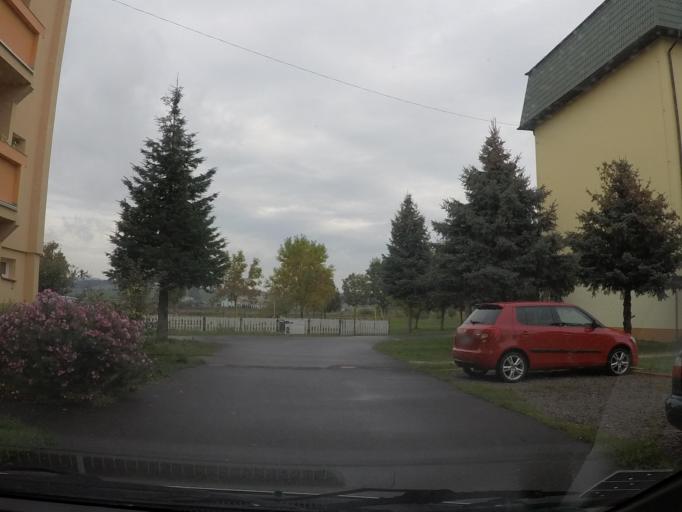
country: SK
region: Banskobystricky
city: Dudince
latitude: 48.1889
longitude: 18.8485
